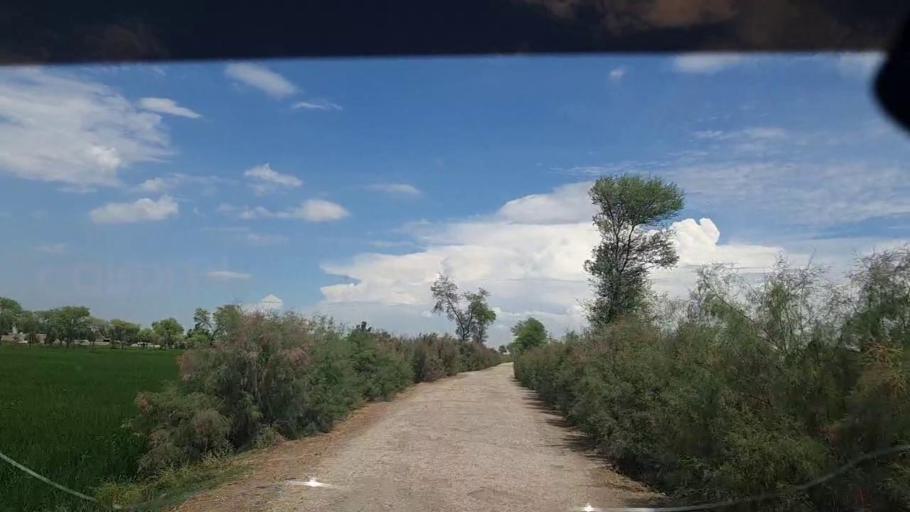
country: PK
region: Sindh
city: Ghauspur
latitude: 28.1489
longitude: 68.9922
